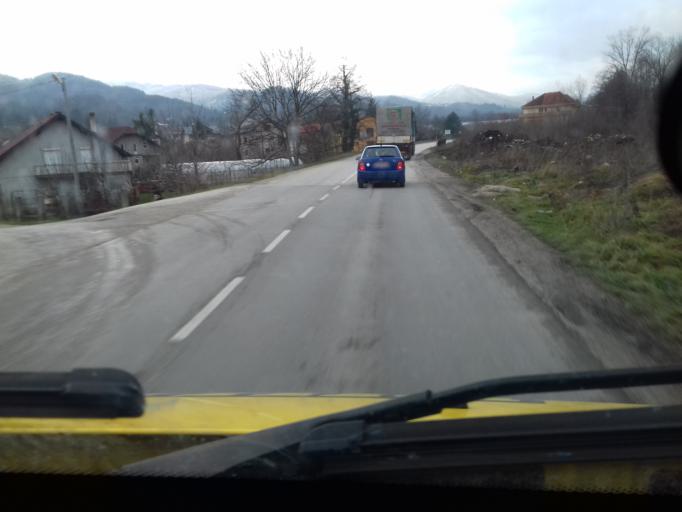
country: BA
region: Federation of Bosnia and Herzegovina
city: Dubravica
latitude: 44.4164
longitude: 18.1246
